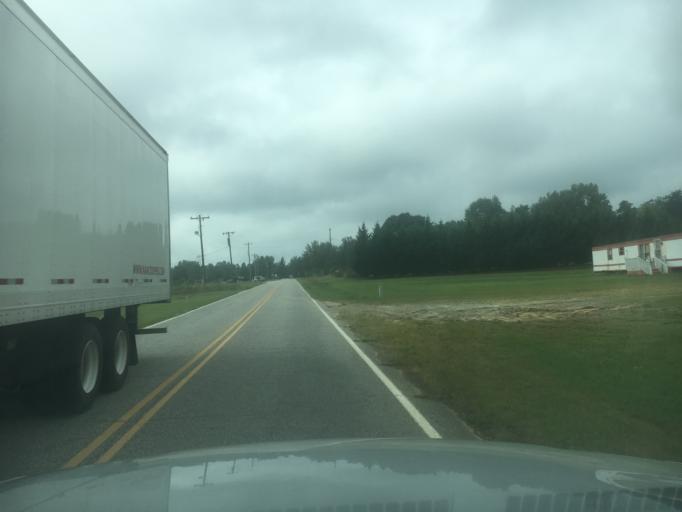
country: US
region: South Carolina
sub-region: Spartanburg County
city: Landrum
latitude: 35.1481
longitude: -82.1025
